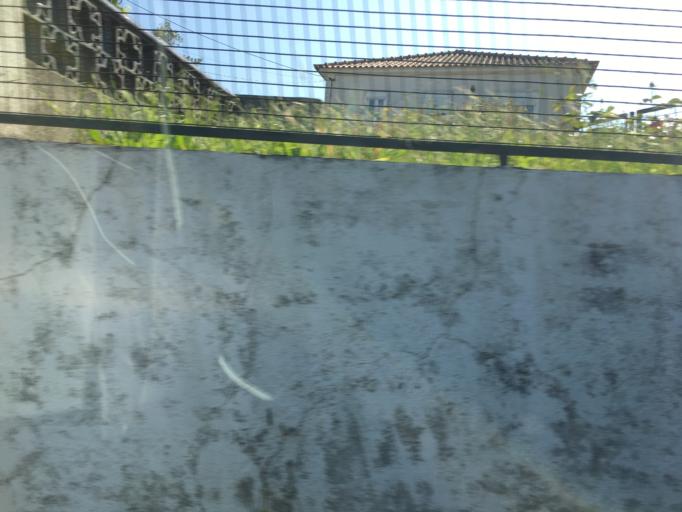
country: PT
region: Lisbon
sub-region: Sintra
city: Sintra
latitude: 38.8057
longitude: -9.3969
